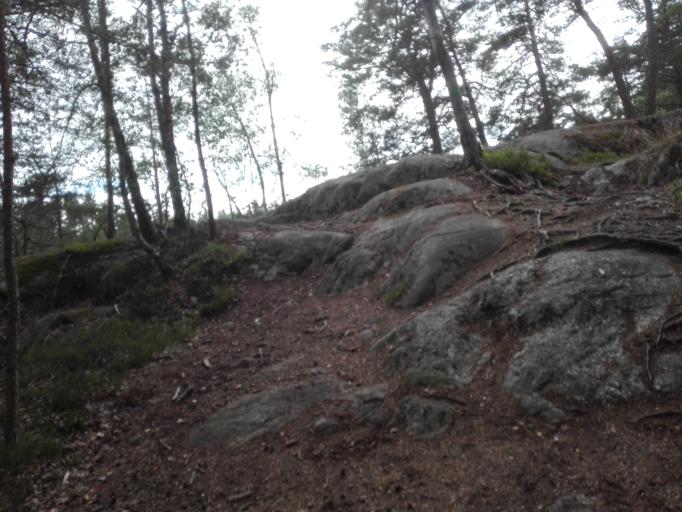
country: SE
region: Stockholm
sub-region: Nacka Kommun
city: Fisksatra
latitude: 59.2828
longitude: 18.2465
